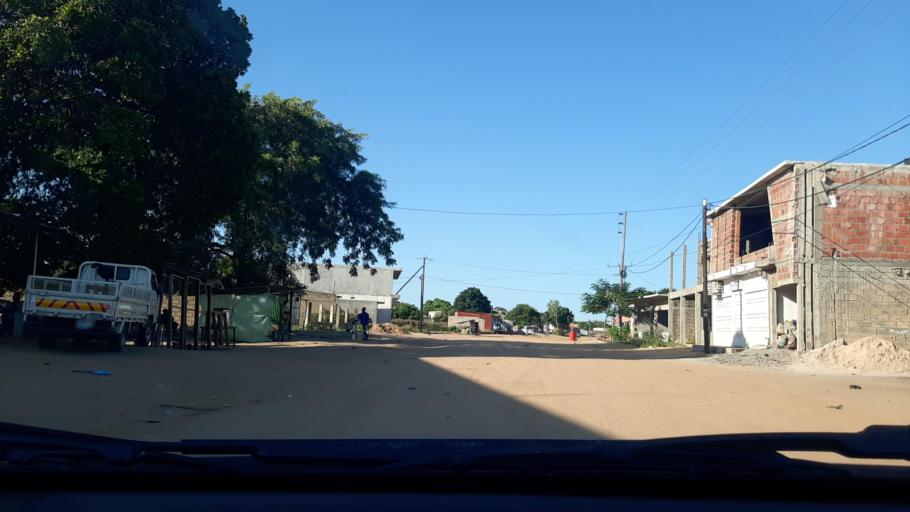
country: MZ
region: Maputo City
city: Maputo
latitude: -25.8016
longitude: 32.5485
